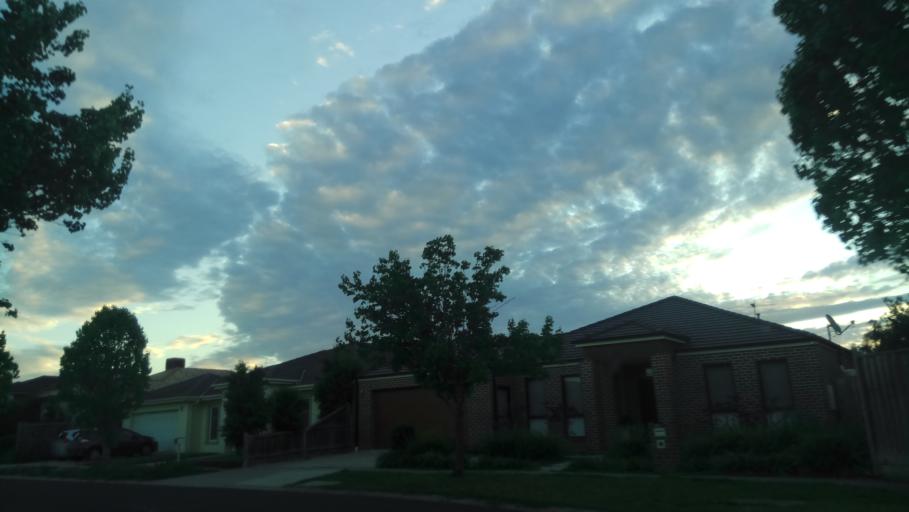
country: AU
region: Victoria
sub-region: Wyndham
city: Point Cook
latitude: -37.9015
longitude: 144.7479
